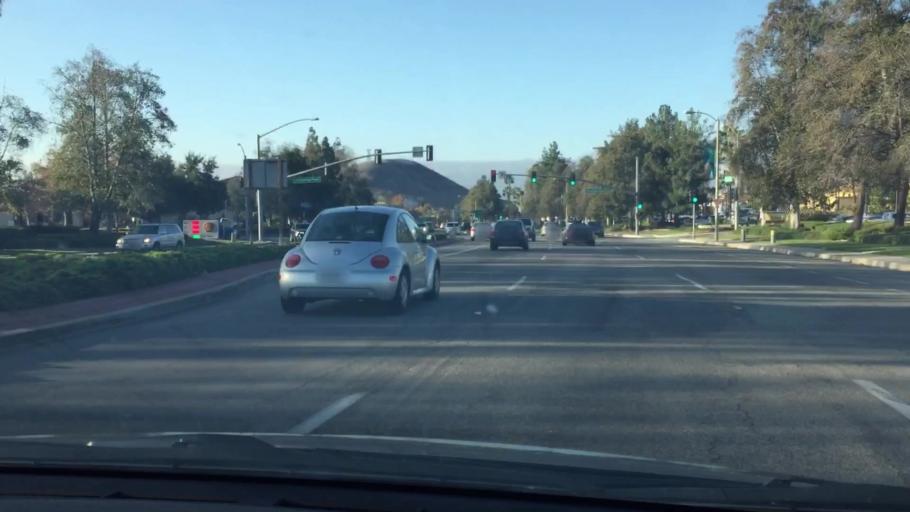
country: US
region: California
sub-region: Orange County
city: Rancho Santa Margarita
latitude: 33.6423
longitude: -117.6046
